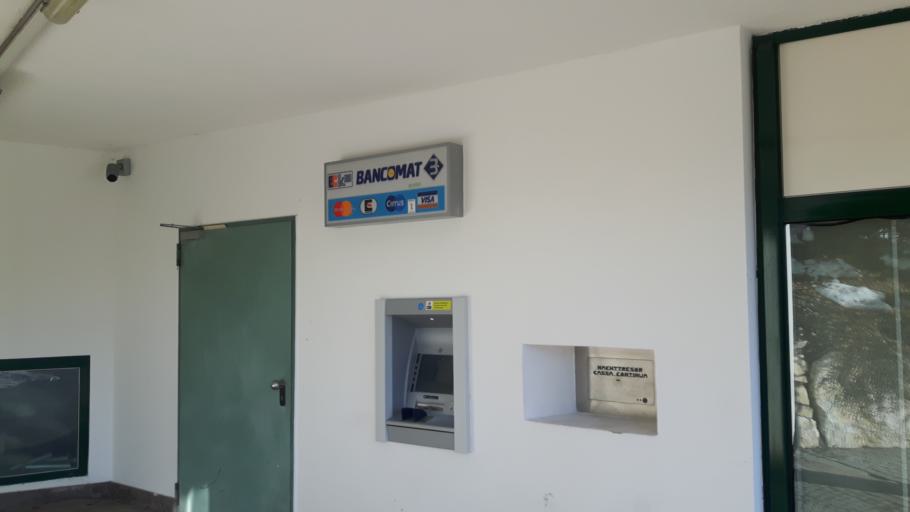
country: IT
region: Trentino-Alto Adige
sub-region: Bolzano
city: Nova Levante
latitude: 46.3834
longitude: 11.5263
